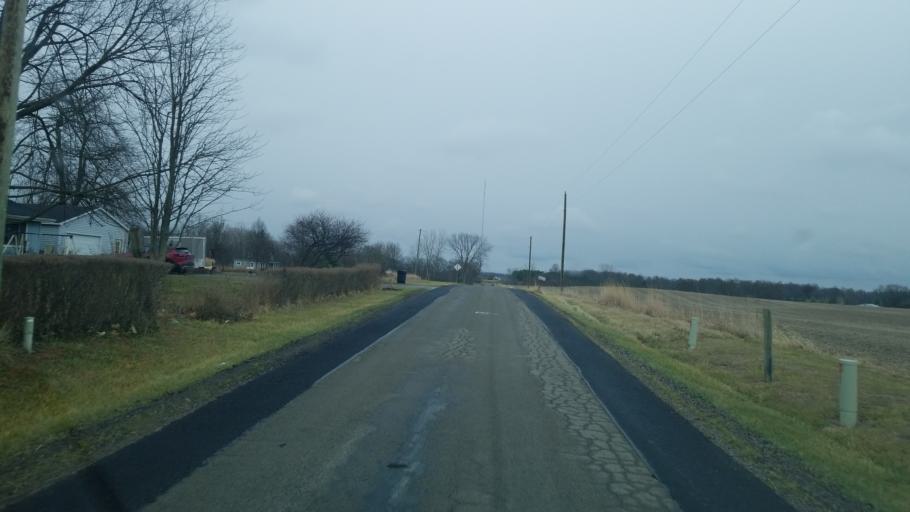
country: US
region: Ohio
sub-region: Union County
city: Marysville
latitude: 40.3060
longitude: -83.3409
